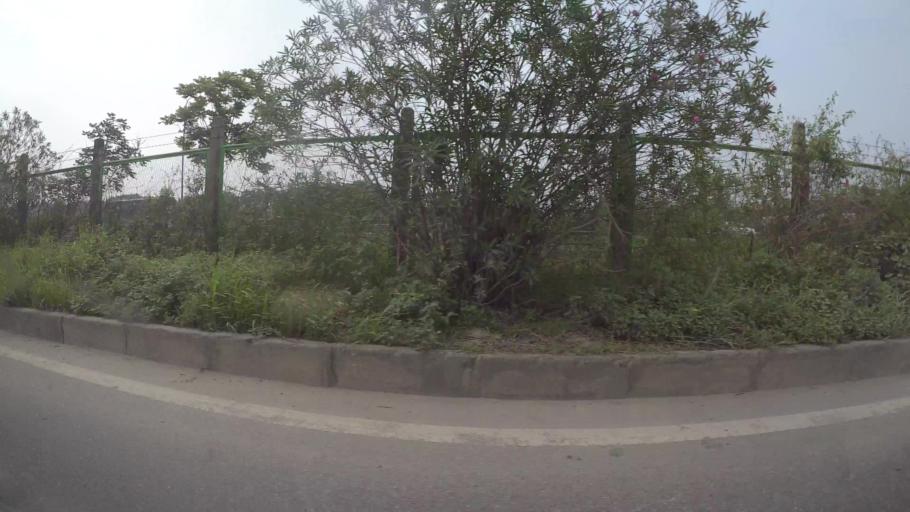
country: VN
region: Ha Noi
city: Quoc Oai
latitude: 21.0041
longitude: 105.6413
